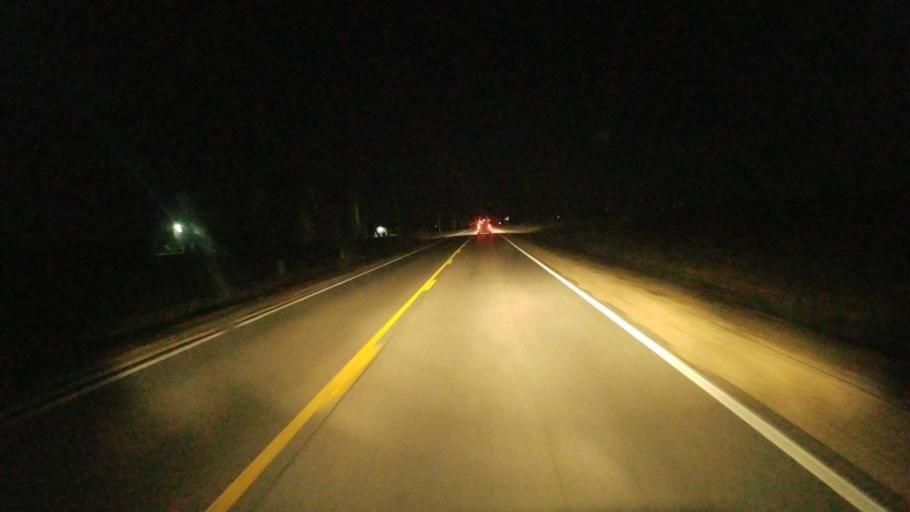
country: US
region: Illinois
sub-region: Henderson County
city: Oquawka
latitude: 40.8234
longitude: -90.9039
